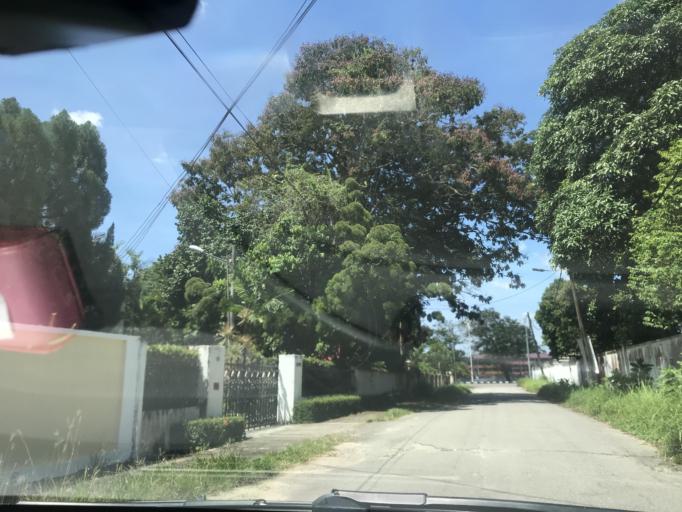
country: MY
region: Kelantan
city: Kota Bharu
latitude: 6.1092
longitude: 102.2526
